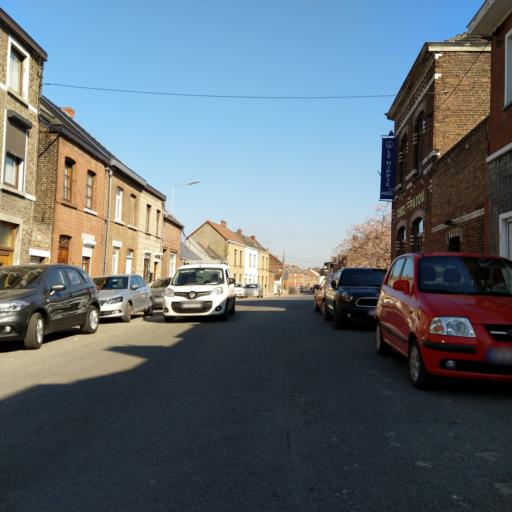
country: BE
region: Wallonia
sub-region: Province du Hainaut
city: Mons
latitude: 50.4665
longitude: 3.9591
